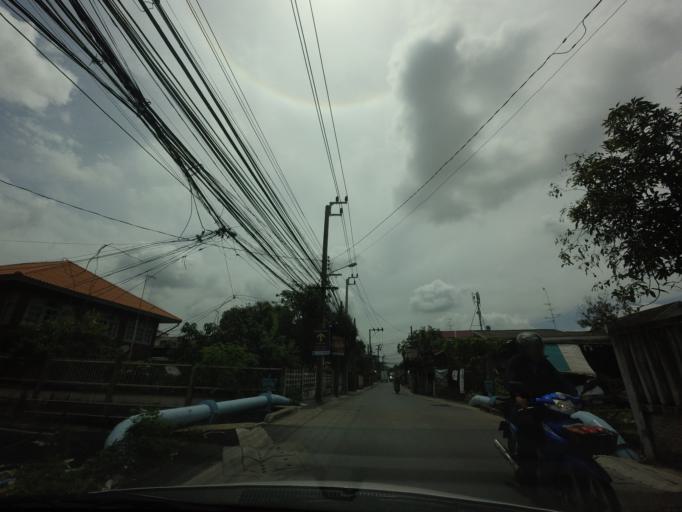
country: TH
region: Bangkok
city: Thung Khru
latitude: 13.6427
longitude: 100.5040
